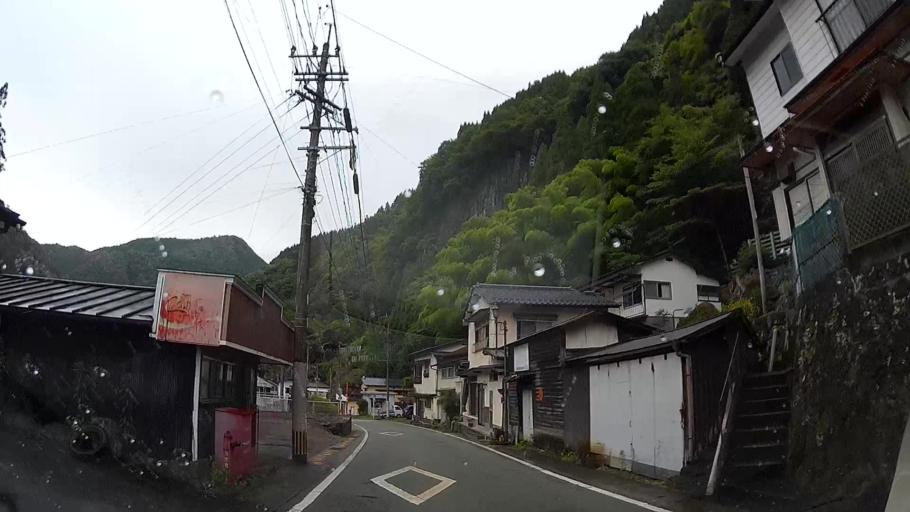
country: JP
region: Oita
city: Tsukawaki
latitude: 33.1805
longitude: 131.0370
